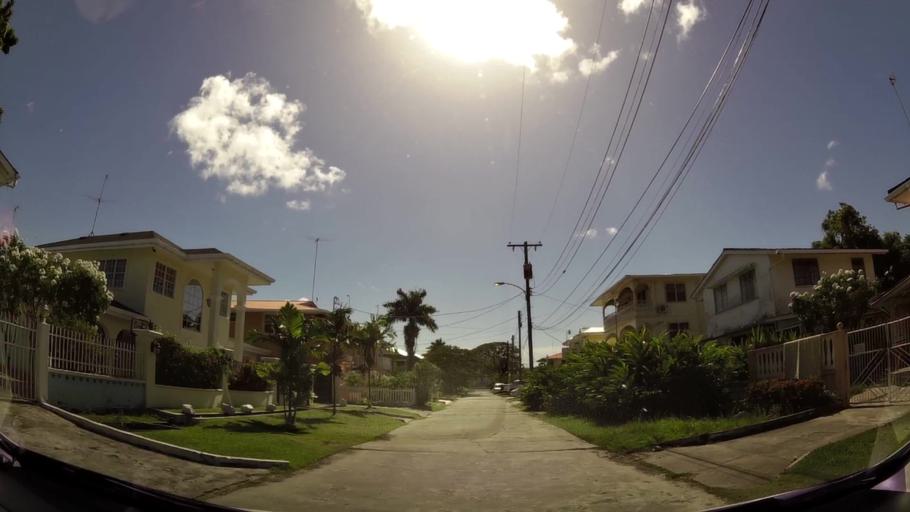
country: GY
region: Demerara-Mahaica
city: Georgetown
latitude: 6.8090
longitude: -58.1389
